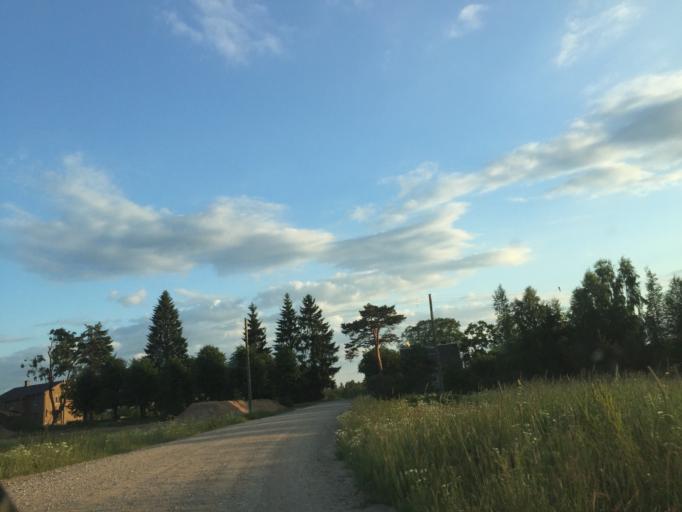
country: LV
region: Sigulda
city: Sigulda
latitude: 57.1176
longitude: 24.9584
